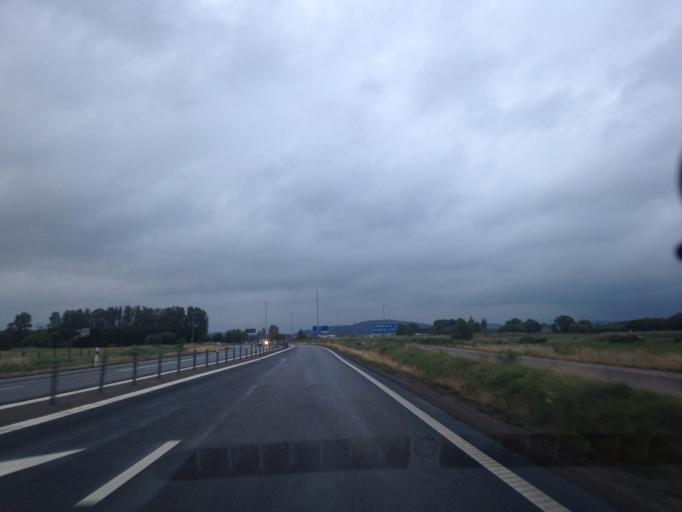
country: SE
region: Halland
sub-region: Varbergs Kommun
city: Varberg
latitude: 57.1437
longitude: 12.2674
